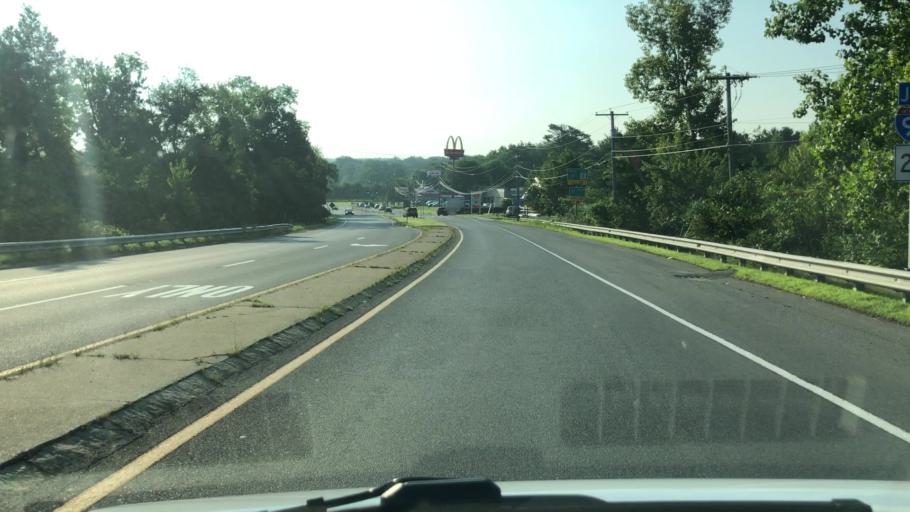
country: US
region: Massachusetts
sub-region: Franklin County
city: Greenfield
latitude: 42.5866
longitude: -72.6277
